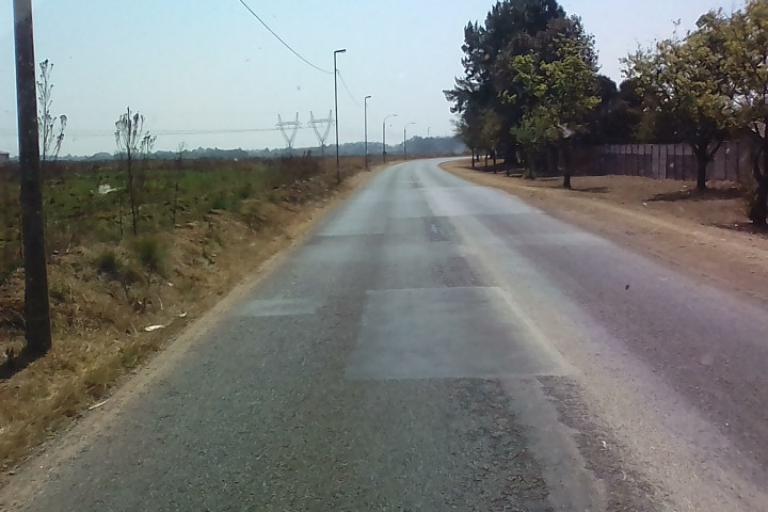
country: ZA
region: Gauteng
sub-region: Ekurhuleni Metropolitan Municipality
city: Benoni
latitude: -26.1476
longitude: 28.2809
